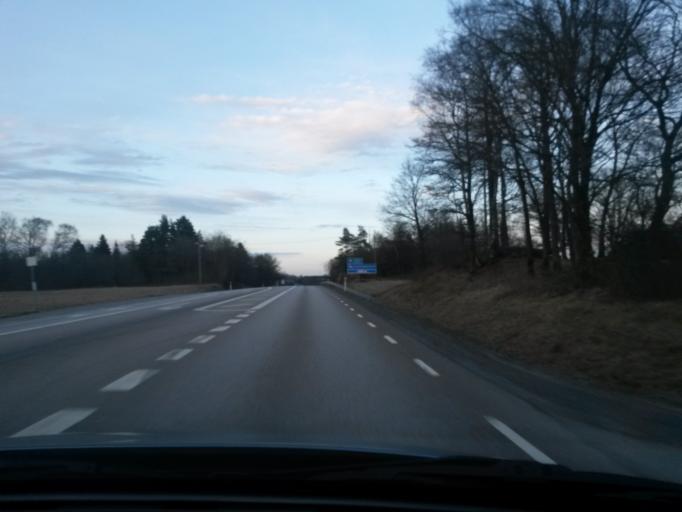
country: SE
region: Vaestra Goetaland
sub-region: Vargarda Kommun
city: Jonstorp
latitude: 58.0006
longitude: 12.7247
